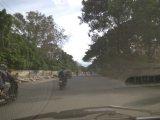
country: IN
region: Karnataka
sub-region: Bangalore Urban
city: Bangalore
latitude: 12.9891
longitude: 77.5504
